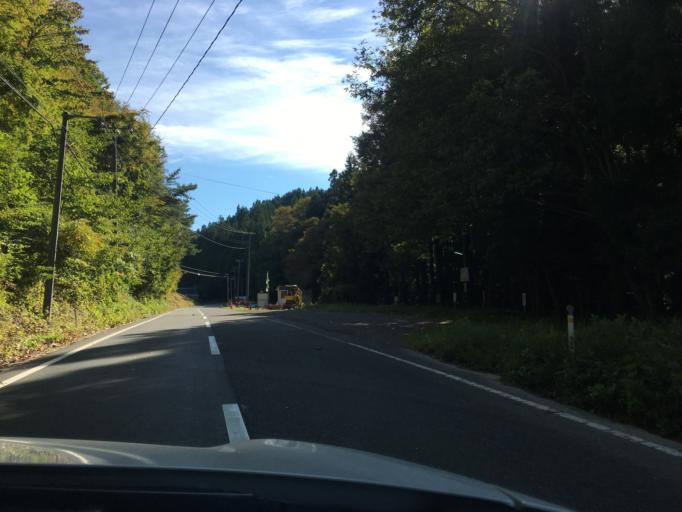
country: JP
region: Fukushima
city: Ishikawa
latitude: 37.1976
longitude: 140.5832
